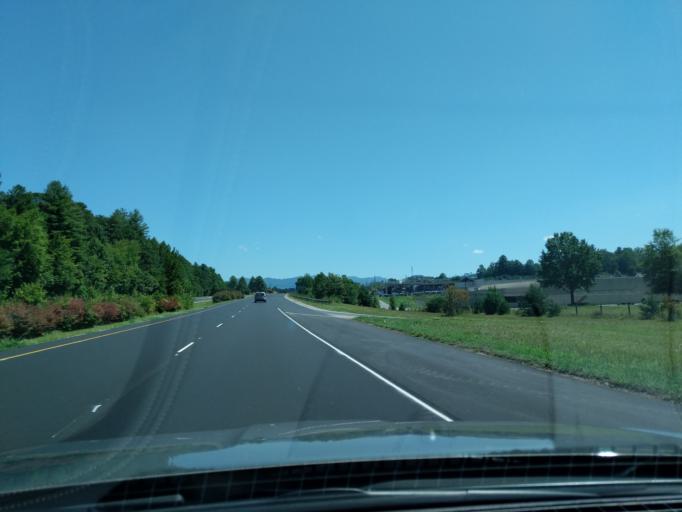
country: US
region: North Carolina
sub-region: Macon County
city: Franklin
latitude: 35.1667
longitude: -83.4000
